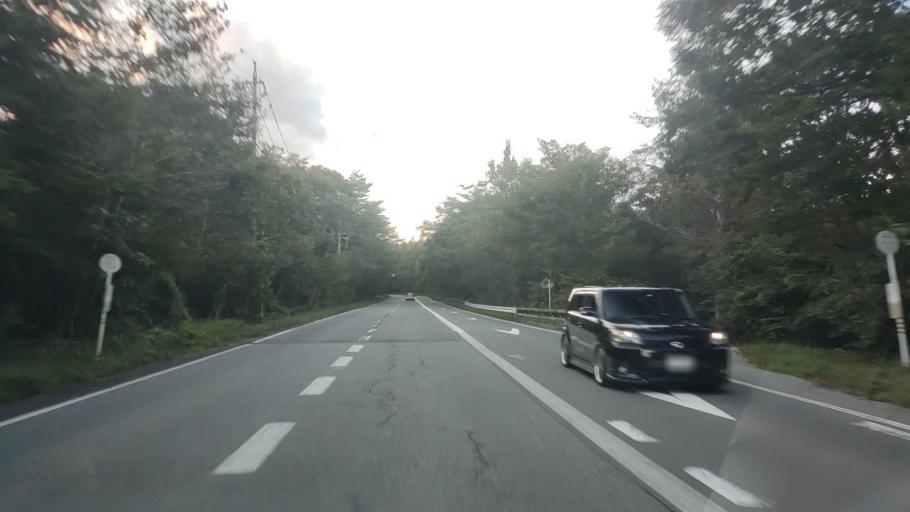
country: JP
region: Nagano
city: Komoro
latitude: 36.3862
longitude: 138.5892
